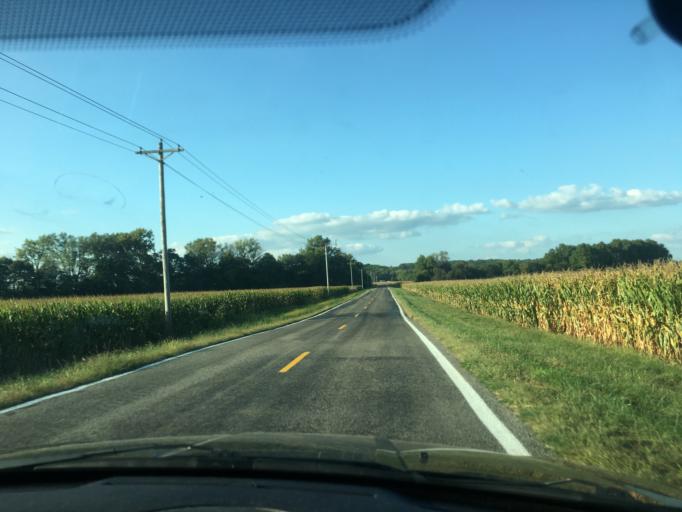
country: US
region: Ohio
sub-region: Logan County
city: West Liberty
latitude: 40.2162
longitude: -83.7784
